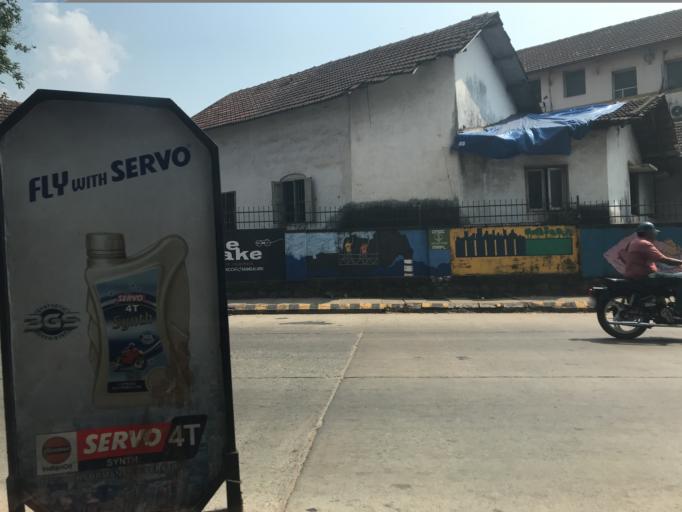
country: IN
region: Karnataka
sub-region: Dakshina Kannada
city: Mangalore
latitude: 12.8673
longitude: 74.8419
